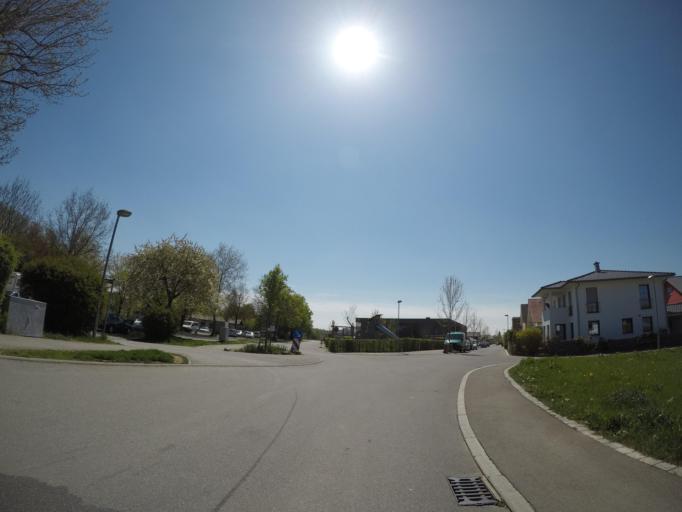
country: DE
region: Baden-Wuerttemberg
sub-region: Tuebingen Region
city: Markdorf
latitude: 47.7138
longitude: 9.3885
